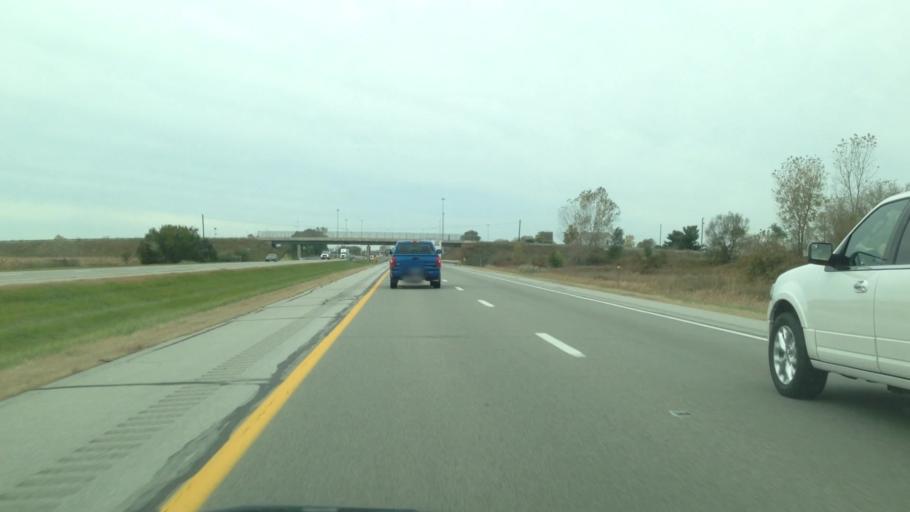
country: US
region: Ohio
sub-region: Fulton County
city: Wauseon
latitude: 41.5926
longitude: -84.1309
